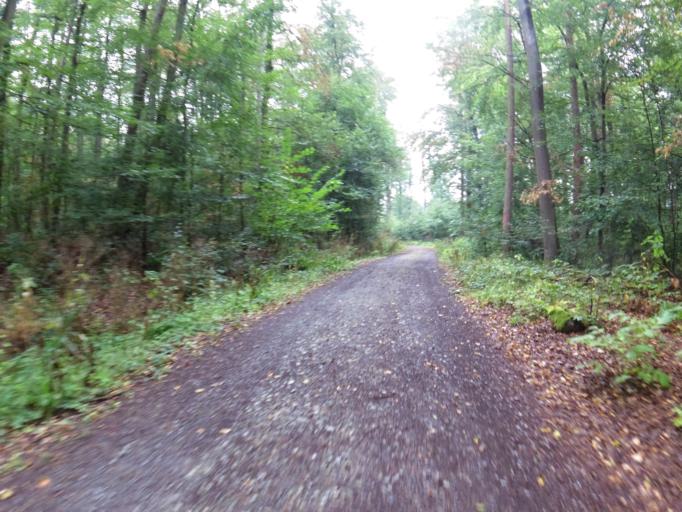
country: DE
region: Bavaria
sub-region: Regierungsbezirk Unterfranken
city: Guntersleben
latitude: 49.8661
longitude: 9.9220
